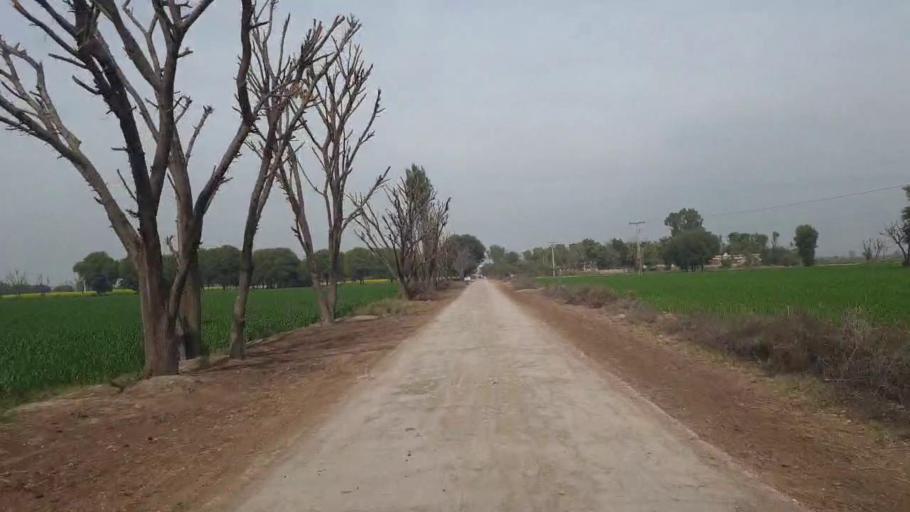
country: PK
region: Sindh
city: Nawabshah
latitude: 26.1208
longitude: 68.4800
